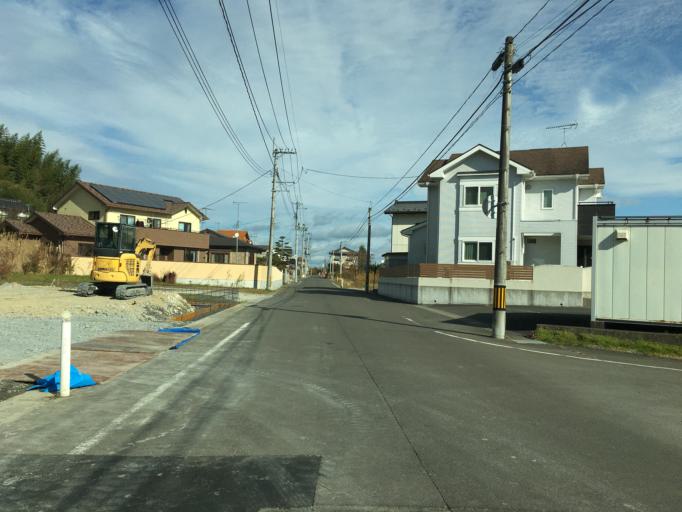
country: JP
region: Miyagi
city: Watari
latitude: 37.9244
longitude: 140.8951
